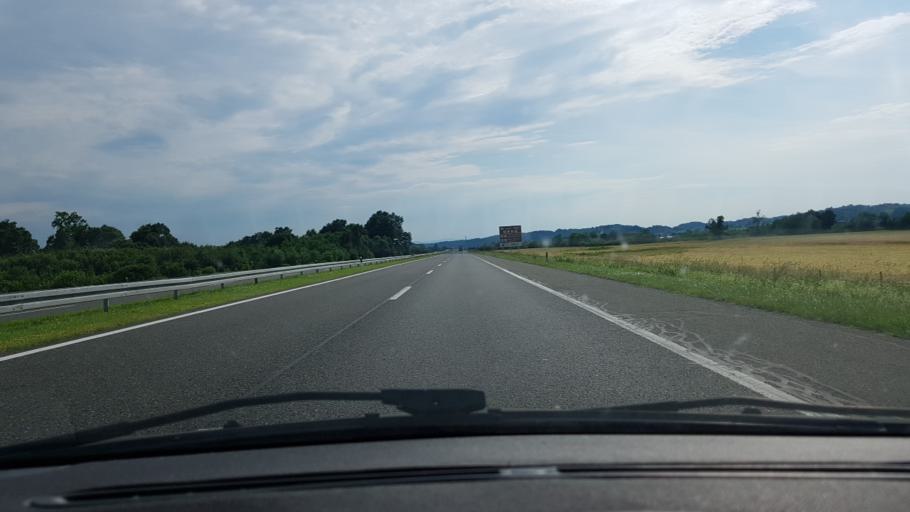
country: HR
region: Krapinsko-Zagorska
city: Zabok
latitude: 46.0152
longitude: 15.8937
